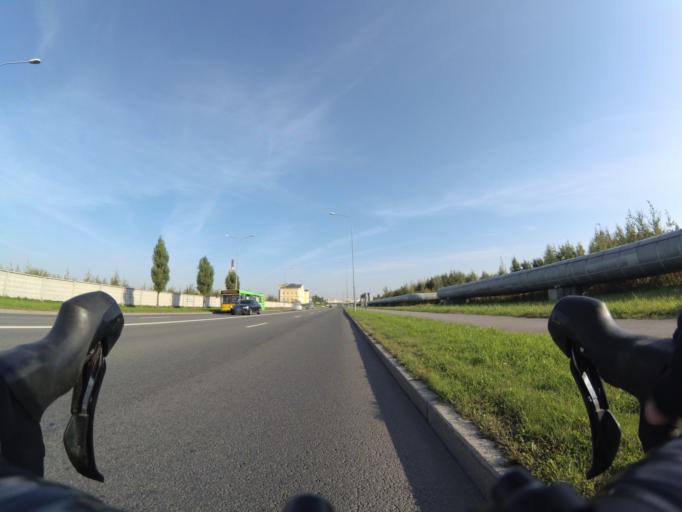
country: RU
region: Leningrad
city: Untolovo
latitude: 59.9936
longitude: 30.2212
